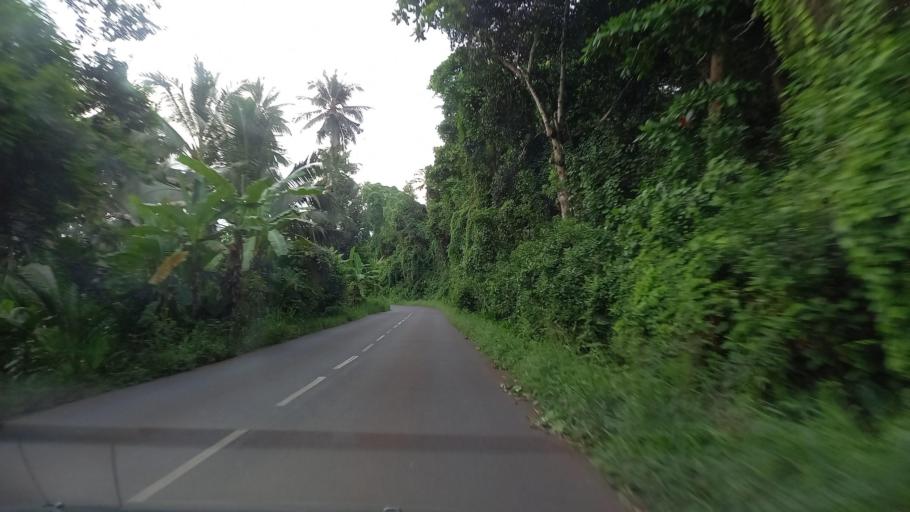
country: YT
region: M'Tsangamouji
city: M'Tsangamouji
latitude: -12.7617
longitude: 45.1021
